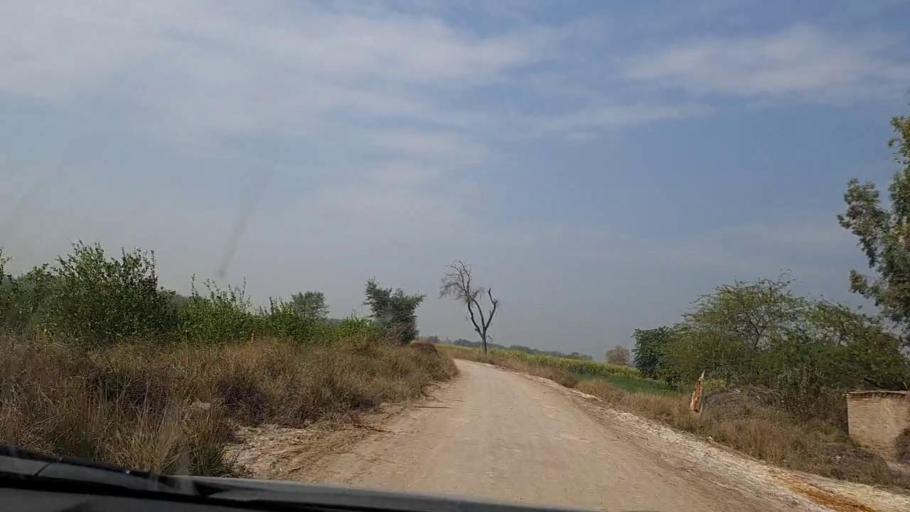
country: PK
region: Sindh
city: Daulatpur
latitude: 26.5327
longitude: 67.9842
